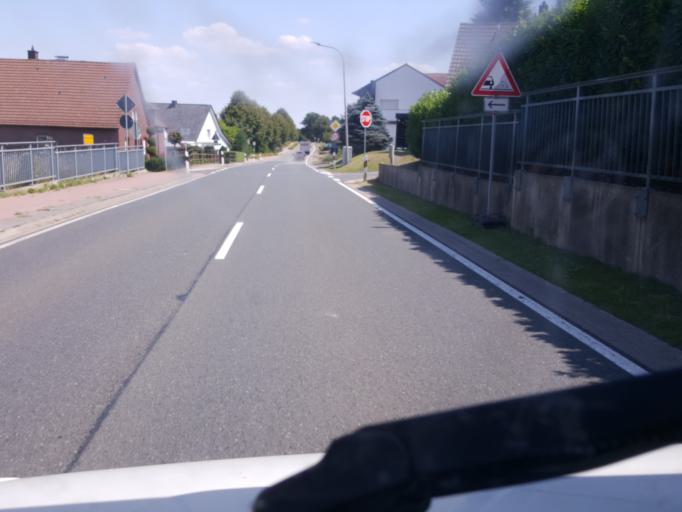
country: DE
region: North Rhine-Westphalia
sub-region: Regierungsbezirk Detmold
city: Hille
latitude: 52.2729
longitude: 8.7797
